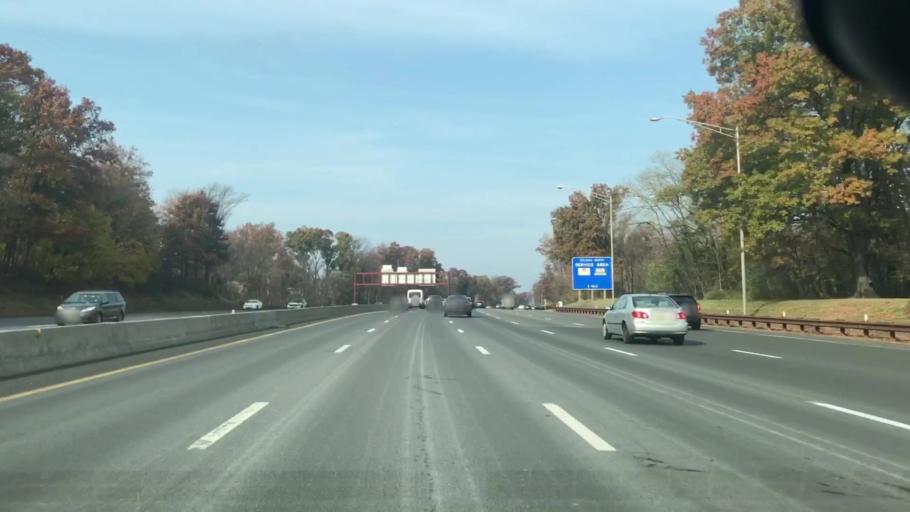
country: US
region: New Jersey
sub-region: Middlesex County
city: Iselin
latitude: 40.5747
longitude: -74.3305
